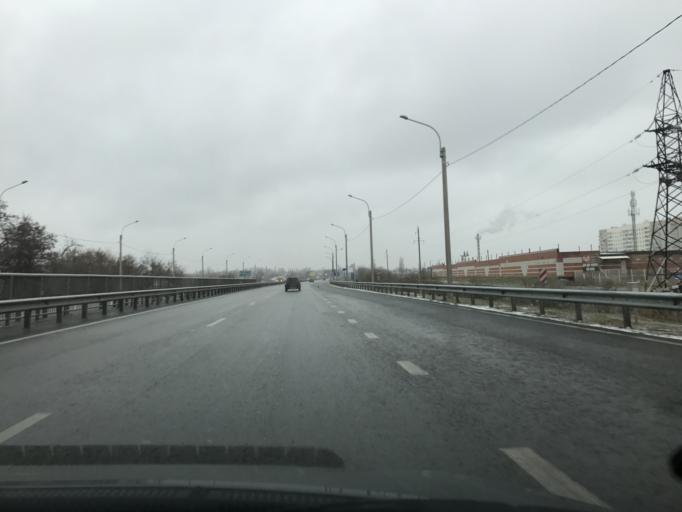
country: RU
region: Rostov
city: Bataysk
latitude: 47.1389
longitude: 39.7763
